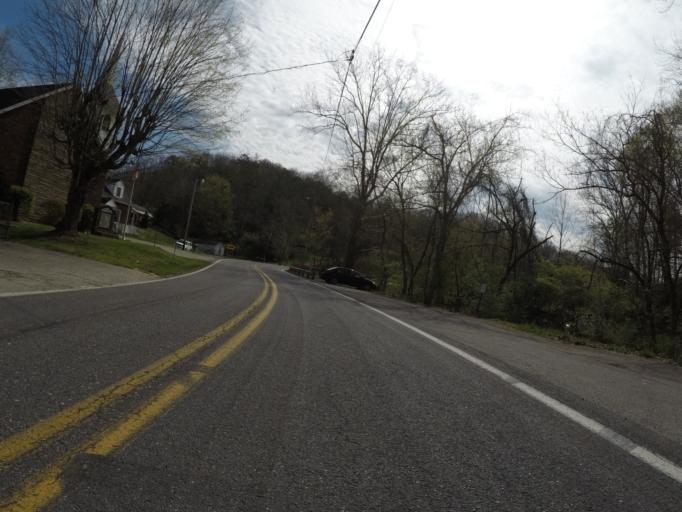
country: US
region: West Virginia
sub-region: Cabell County
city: Pea Ridge
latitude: 38.3648
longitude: -82.3749
